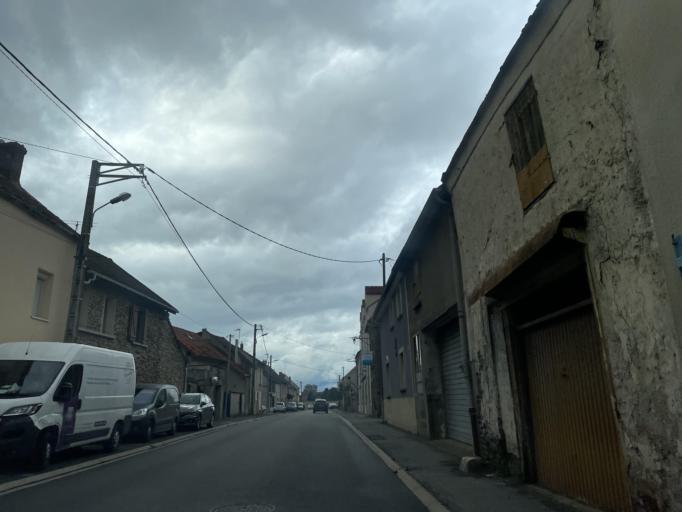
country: FR
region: Ile-de-France
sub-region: Departement de Seine-et-Marne
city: Saint-Jean-les-Deux-Jumeaux
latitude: 48.8995
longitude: 3.0379
